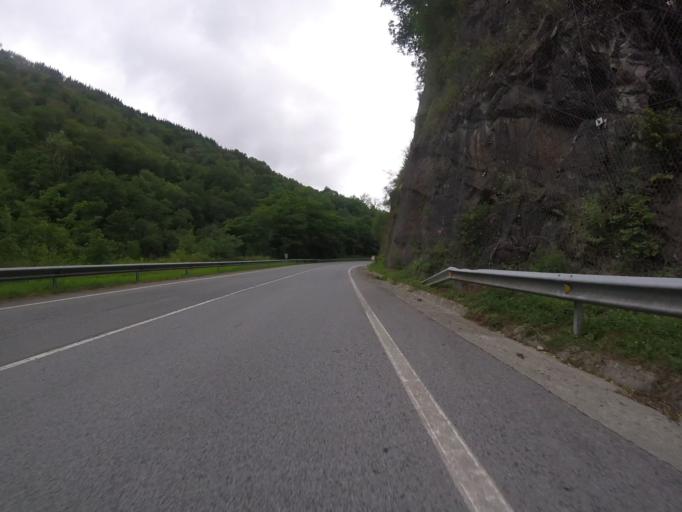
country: ES
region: Navarre
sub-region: Provincia de Navarra
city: Zubieta
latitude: 43.1121
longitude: -1.7619
